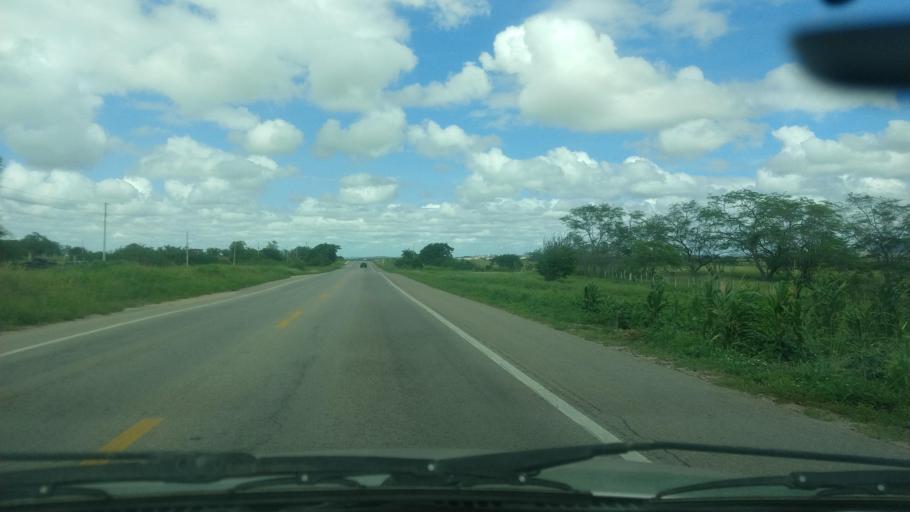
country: BR
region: Rio Grande do Norte
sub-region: Tangara
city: Tangara
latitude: -6.1760
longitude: -35.7671
